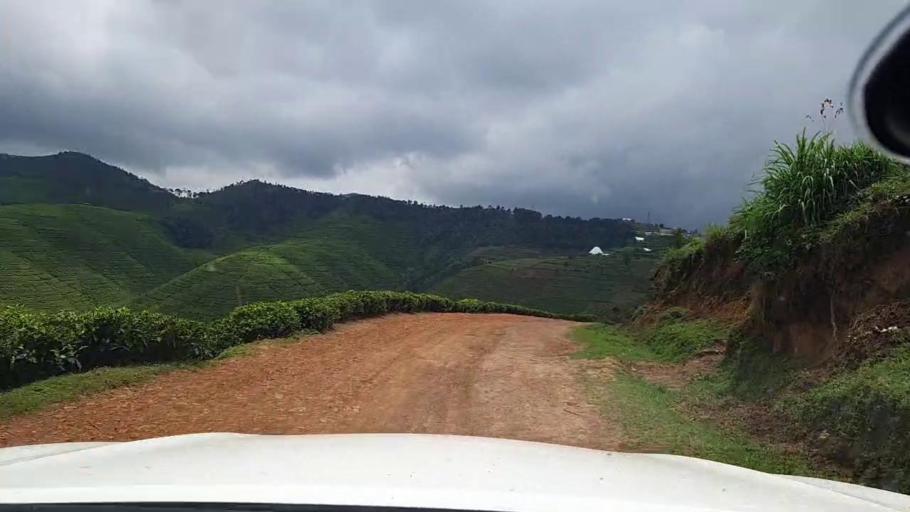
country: RW
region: Western Province
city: Kibuye
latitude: -2.1722
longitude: 29.4375
